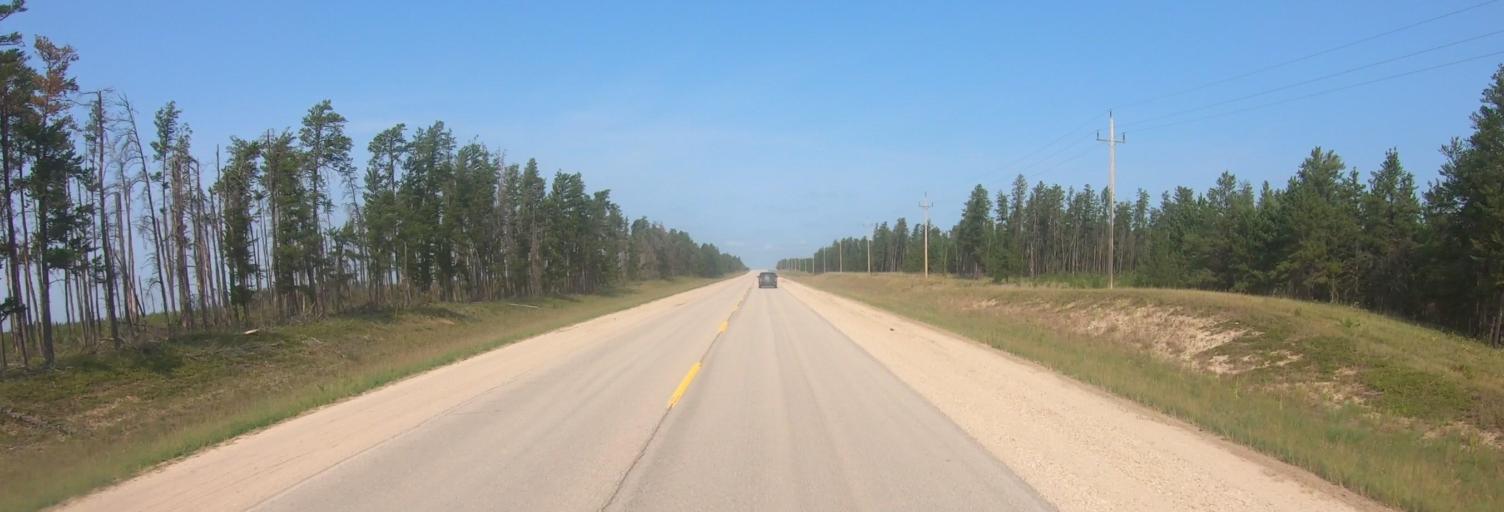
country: US
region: Minnesota
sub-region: Roseau County
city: Roseau
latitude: 49.1283
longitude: -96.0749
